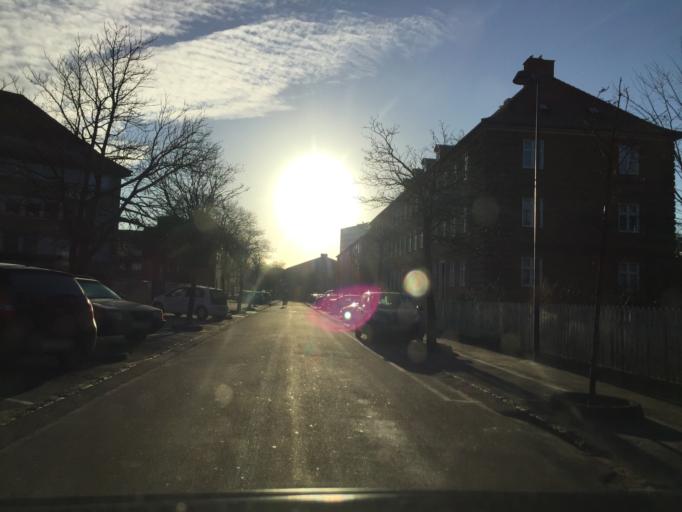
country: DK
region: Capital Region
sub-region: Kobenhavn
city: Vanlose
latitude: 55.6607
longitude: 12.5046
